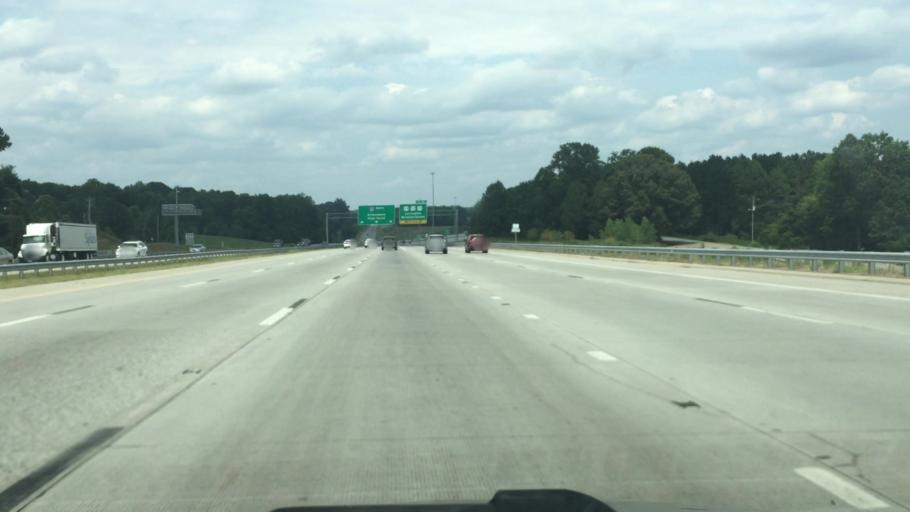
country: US
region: North Carolina
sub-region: Davidson County
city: Tyro
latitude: 35.7663
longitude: -80.3331
